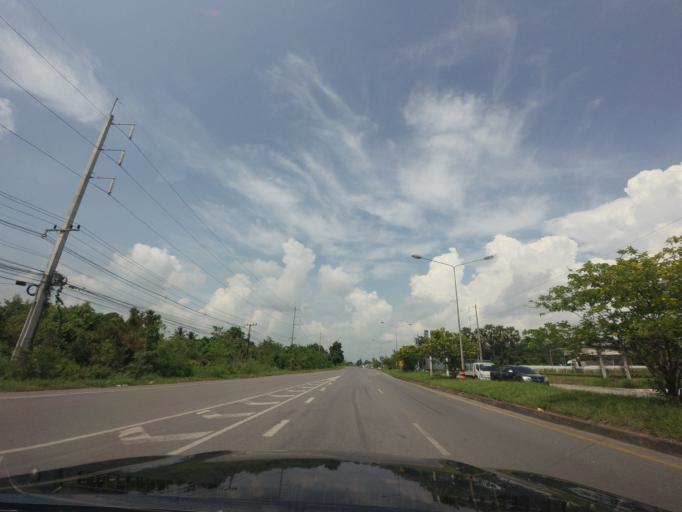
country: TH
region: Khon Kaen
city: Ban Fang
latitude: 16.4498
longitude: 102.7128
